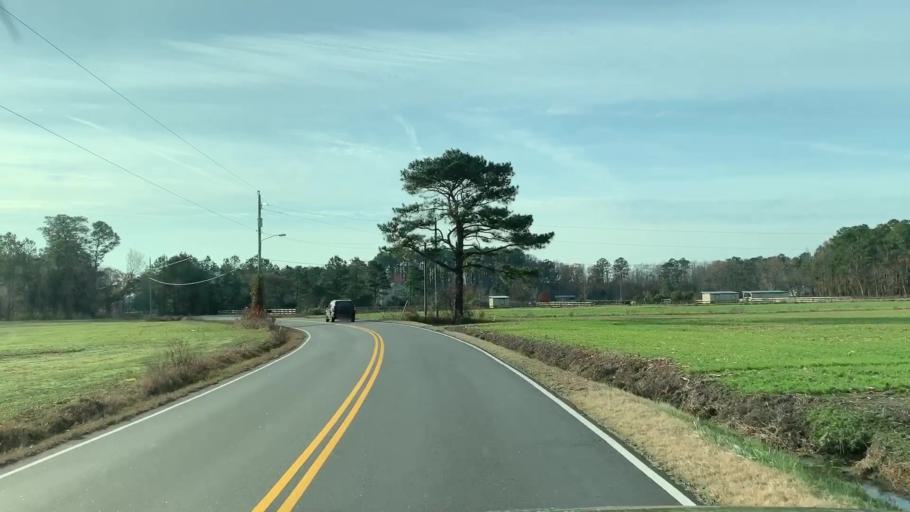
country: US
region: Virginia
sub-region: City of Virginia Beach
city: Virginia Beach
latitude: 36.7147
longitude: -76.0497
